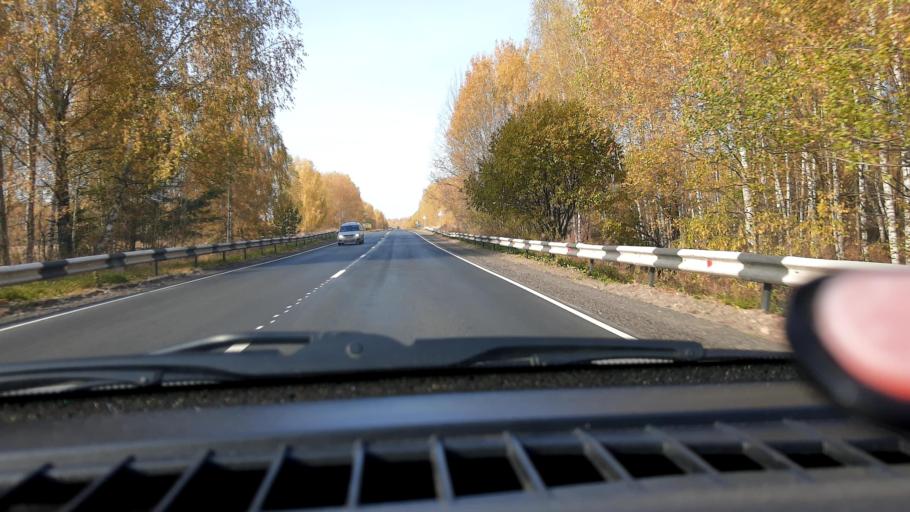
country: RU
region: Nizjnij Novgorod
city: Novaya Balakhna
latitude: 56.5678
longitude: 43.7159
